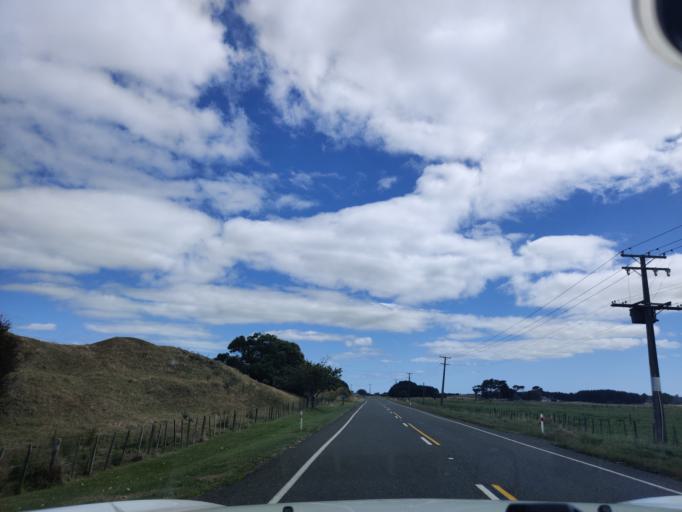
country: NZ
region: Manawatu-Wanganui
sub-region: Horowhenua District
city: Foxton
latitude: -40.4070
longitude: 175.3752
